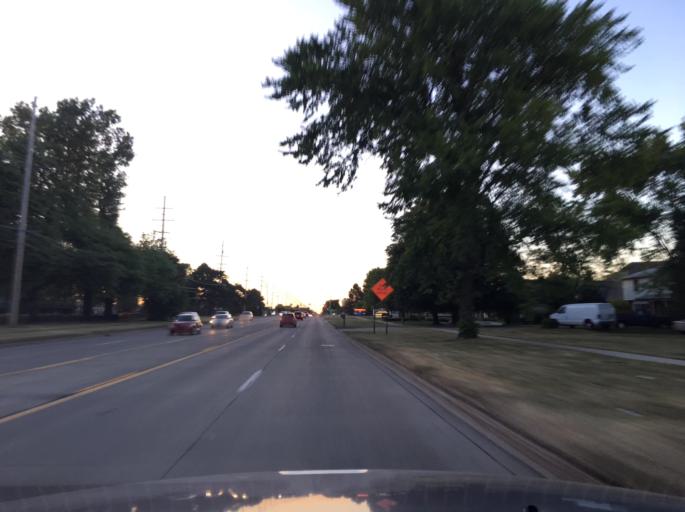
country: US
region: Michigan
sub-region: Macomb County
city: Clinton
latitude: 42.5811
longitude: -82.9517
